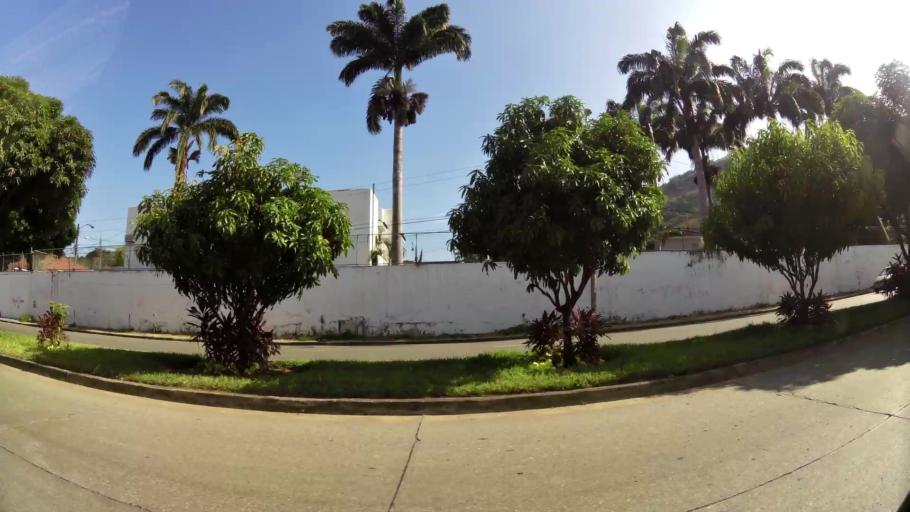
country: EC
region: Guayas
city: Guayaquil
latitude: -2.1718
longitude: -79.9418
